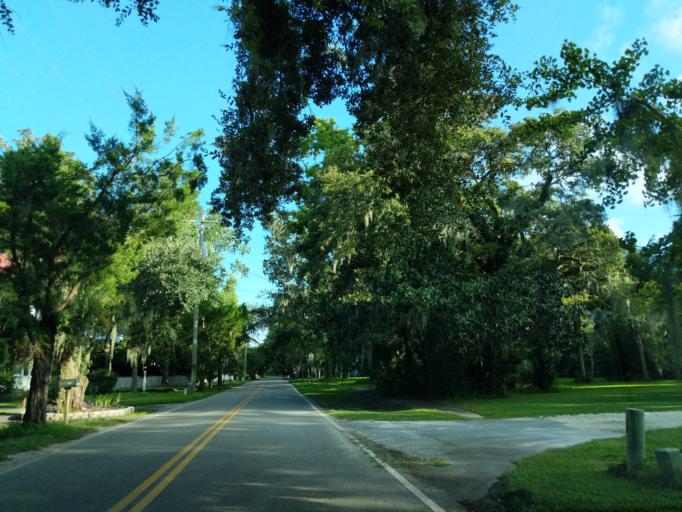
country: US
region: South Carolina
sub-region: Charleston County
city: Awendaw
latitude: 33.0832
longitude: -79.4596
